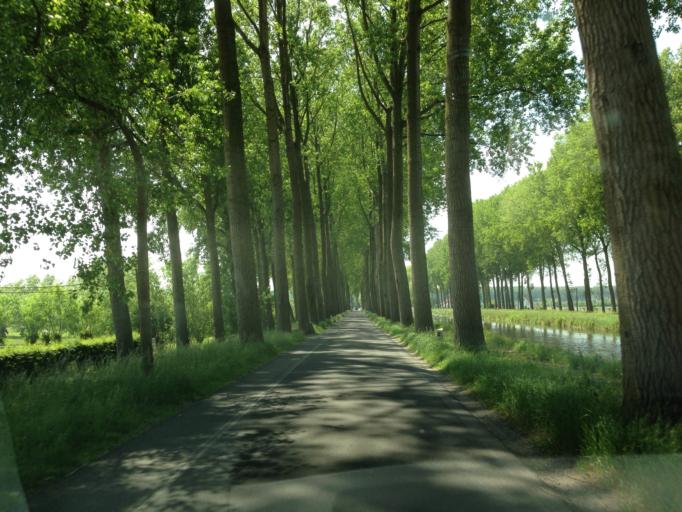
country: BE
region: Flanders
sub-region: Provincie West-Vlaanderen
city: Damme
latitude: 51.2753
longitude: 3.3079
